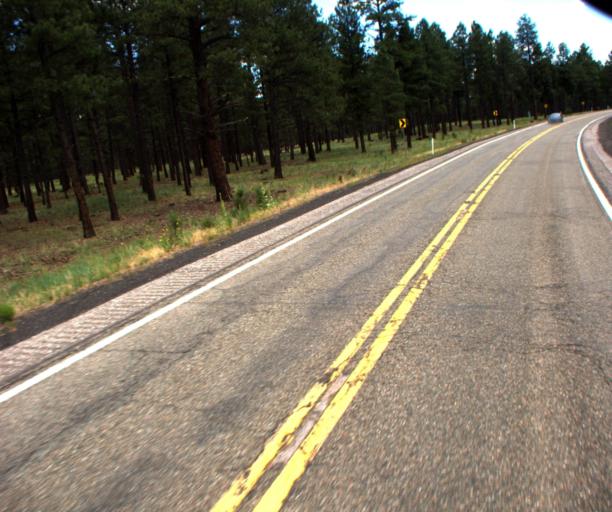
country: US
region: Arizona
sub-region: Coconino County
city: Flagstaff
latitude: 35.2798
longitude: -111.7468
